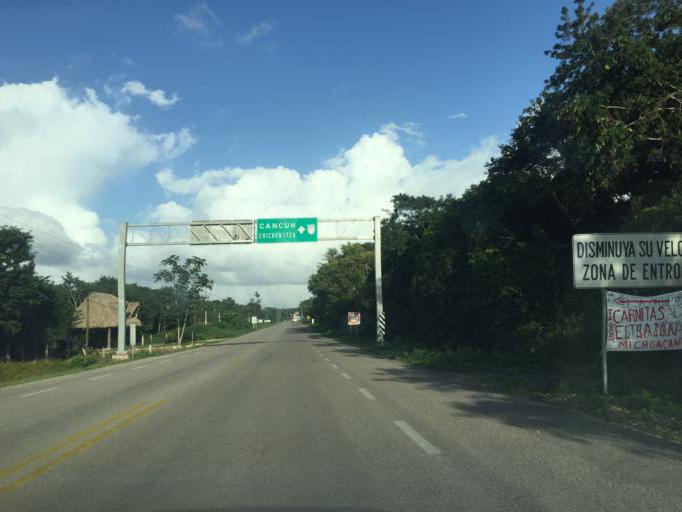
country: MX
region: Quintana Roo
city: Coba
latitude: 20.5058
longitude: -87.7230
